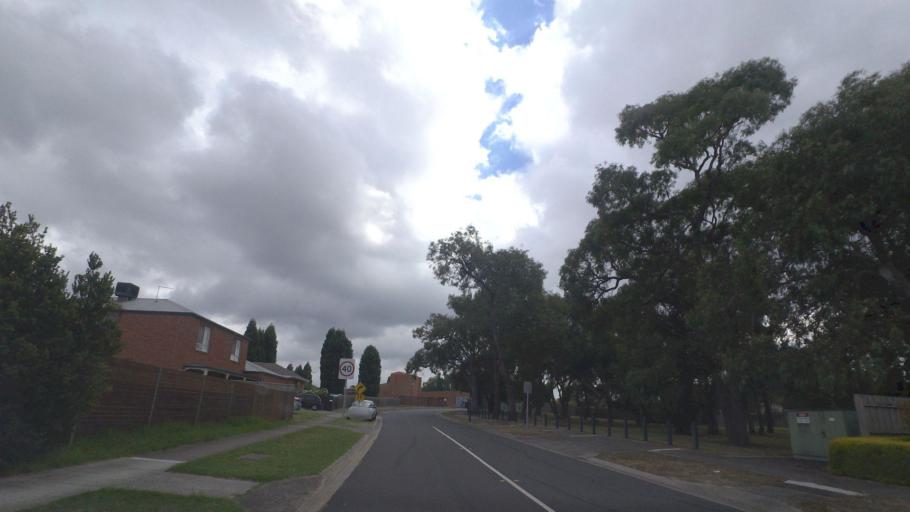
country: AU
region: Victoria
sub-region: Knox
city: Scoresby
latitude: -37.8909
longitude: 145.2276
